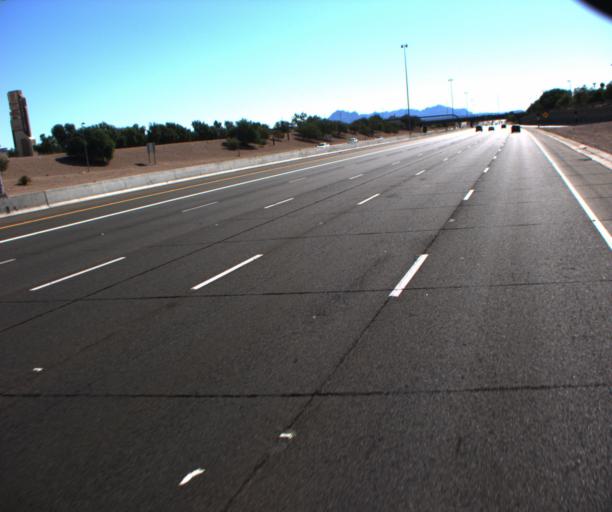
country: US
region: Arizona
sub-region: Maricopa County
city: Gilbert
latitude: 33.3864
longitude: -111.6834
